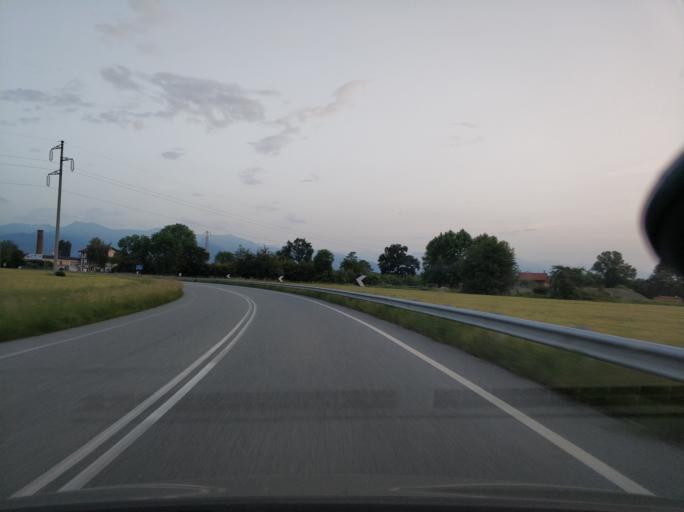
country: IT
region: Piedmont
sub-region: Provincia di Torino
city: San Maurizio
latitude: 45.2163
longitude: 7.6429
